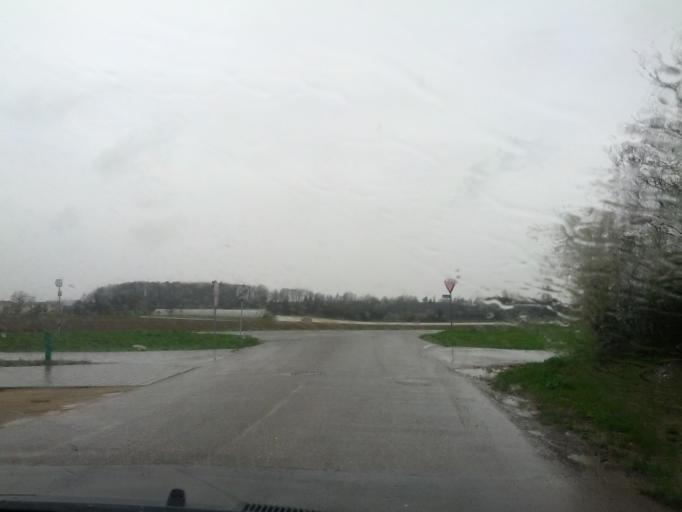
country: DE
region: Baden-Wuerttemberg
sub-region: Freiburg Region
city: Bad Krozingen
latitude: 47.9113
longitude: 7.6949
